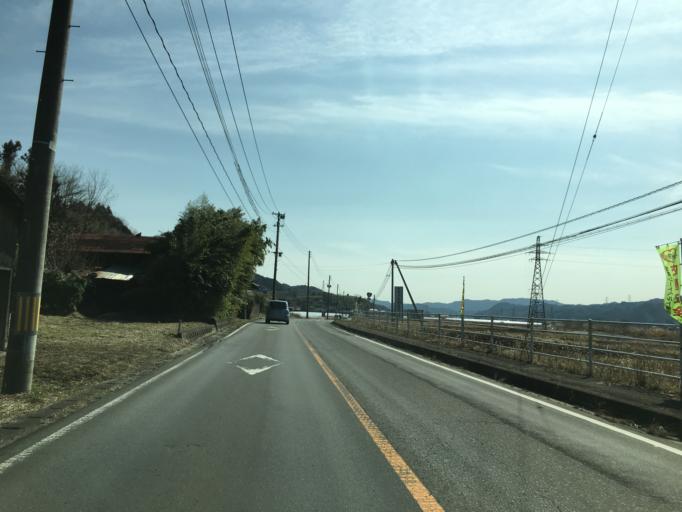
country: JP
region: Ibaraki
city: Daigo
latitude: 36.9244
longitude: 140.4151
